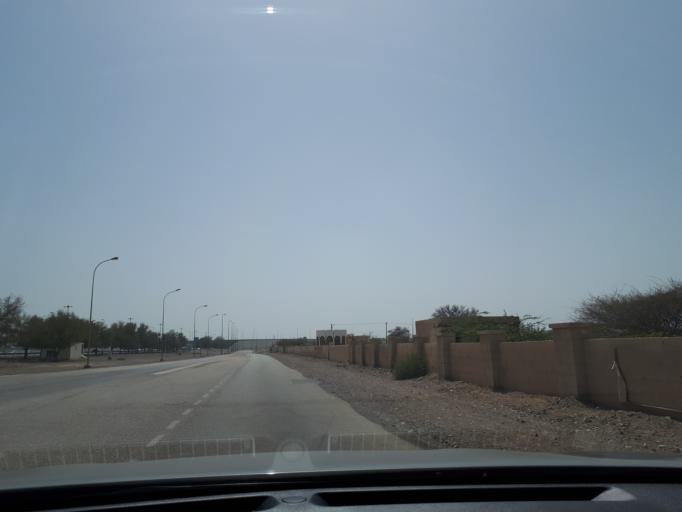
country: OM
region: Al Batinah
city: Barka'
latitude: 23.6892
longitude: 58.0327
